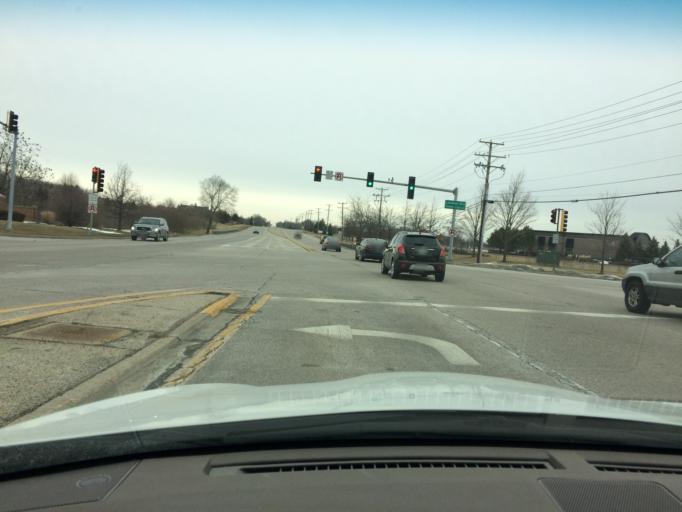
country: US
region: Illinois
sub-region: Cook County
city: South Barrington
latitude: 42.0740
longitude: -88.1410
